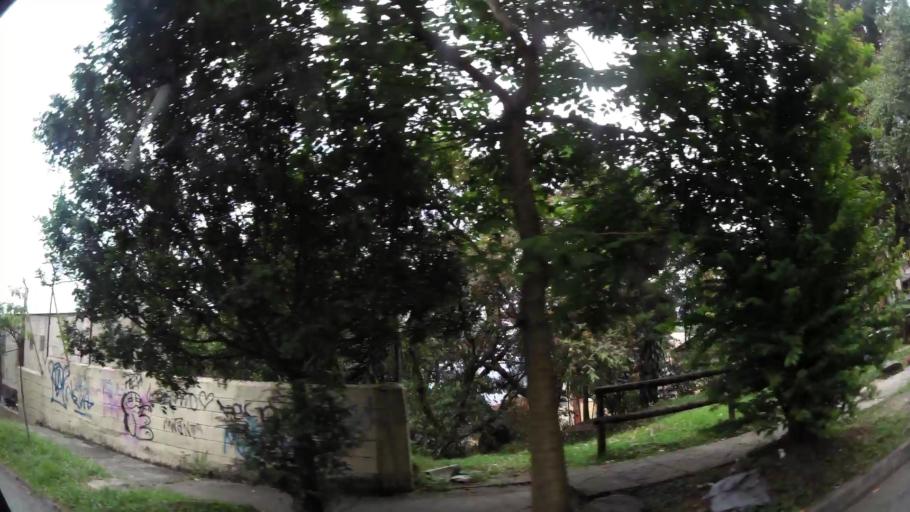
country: CO
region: Antioquia
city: Medellin
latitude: 6.2317
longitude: -75.5507
